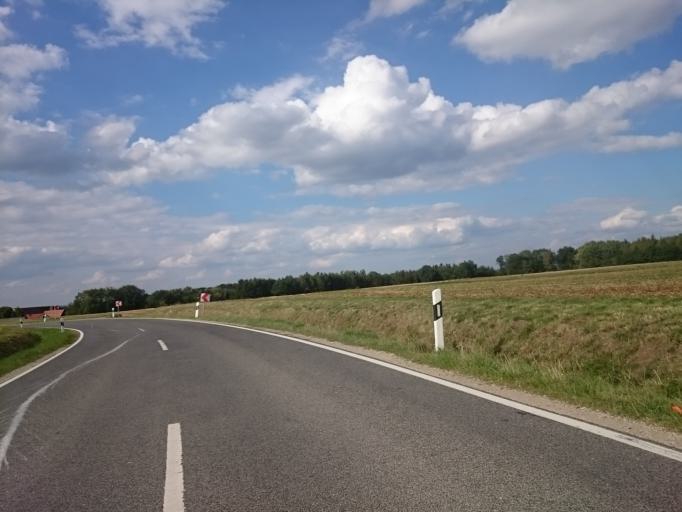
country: DE
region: Bavaria
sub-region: Regierungsbezirk Mittelfranken
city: Heideck
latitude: 49.1281
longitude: 11.1554
